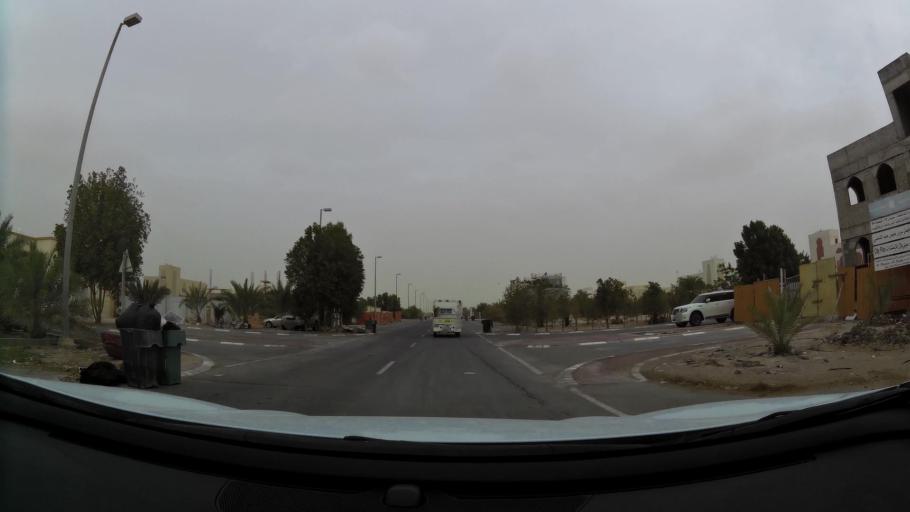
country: AE
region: Abu Dhabi
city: Abu Dhabi
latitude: 24.3782
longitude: 54.7025
